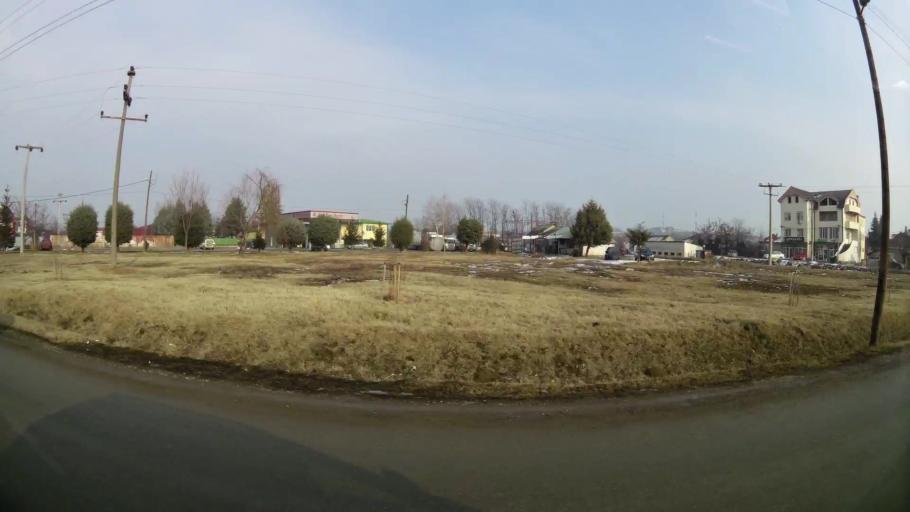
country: MK
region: Ilinden
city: Marino
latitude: 41.9902
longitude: 21.5865
